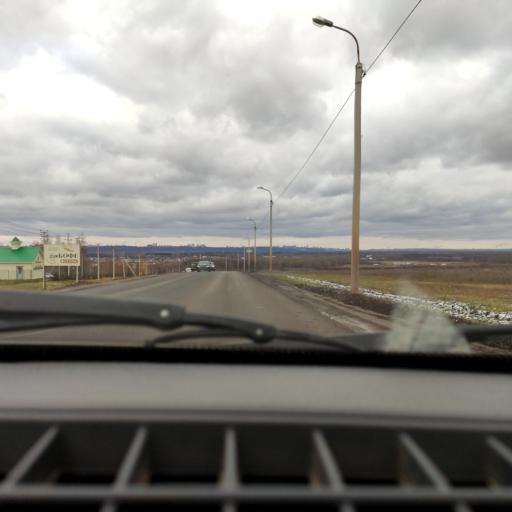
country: RU
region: Bashkortostan
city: Kabakovo
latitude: 54.6351
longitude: 56.0946
